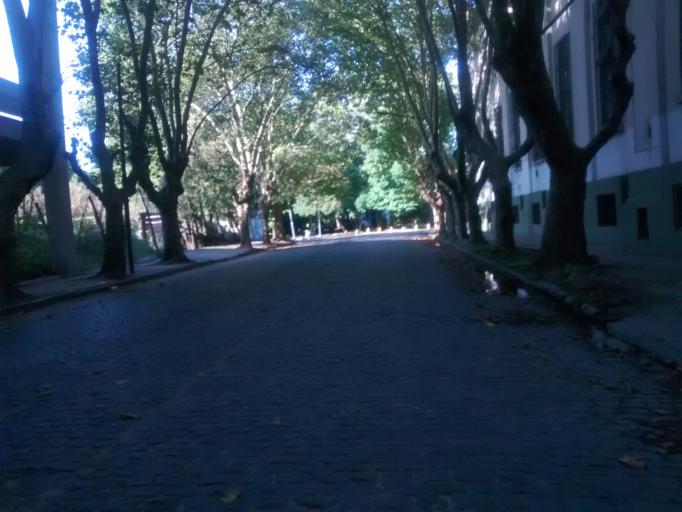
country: AR
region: Buenos Aires
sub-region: Partido de La Plata
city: La Plata
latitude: -34.9125
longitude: -57.9380
